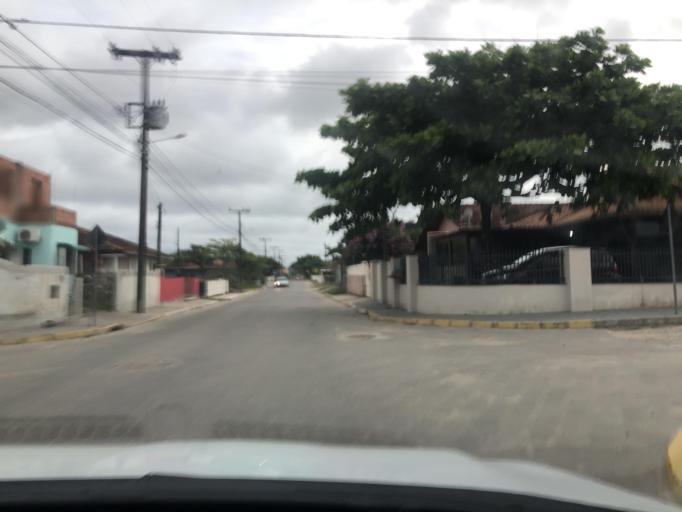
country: BR
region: Santa Catarina
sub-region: Sao Francisco Do Sul
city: Sao Francisco do Sul
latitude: -26.2309
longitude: -48.5200
